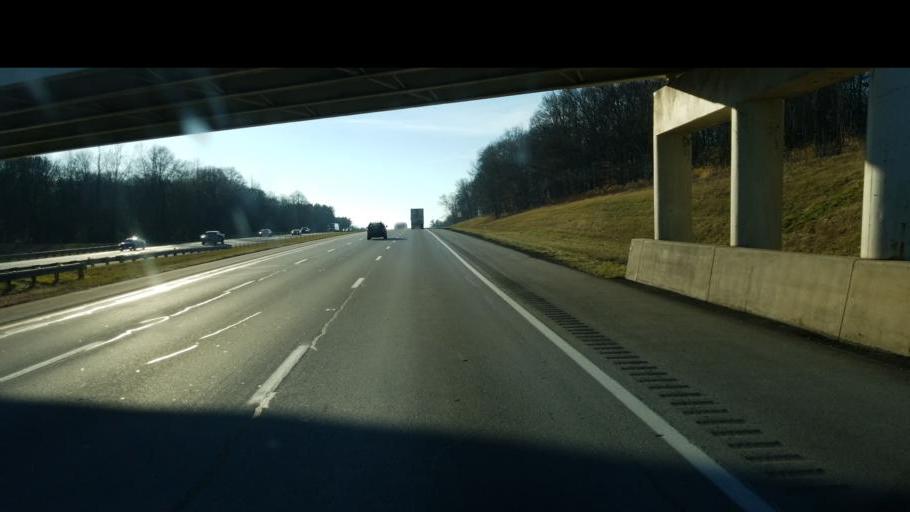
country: US
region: Ohio
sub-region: Medina County
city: Westfield Center
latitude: 41.0229
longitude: -81.9107
